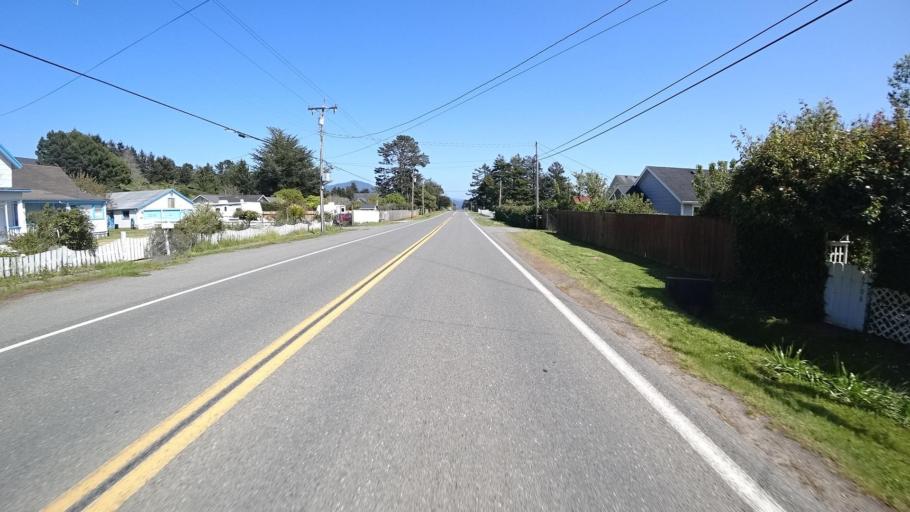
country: US
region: California
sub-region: Humboldt County
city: Hydesville
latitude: 40.5491
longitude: -124.1035
